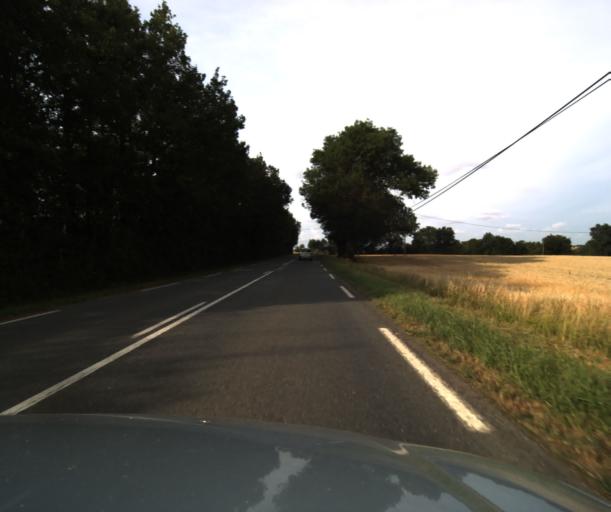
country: FR
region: Midi-Pyrenees
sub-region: Departement du Tarn-et-Garonne
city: Beaumont-de-Lomagne
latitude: 43.8245
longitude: 0.9150
